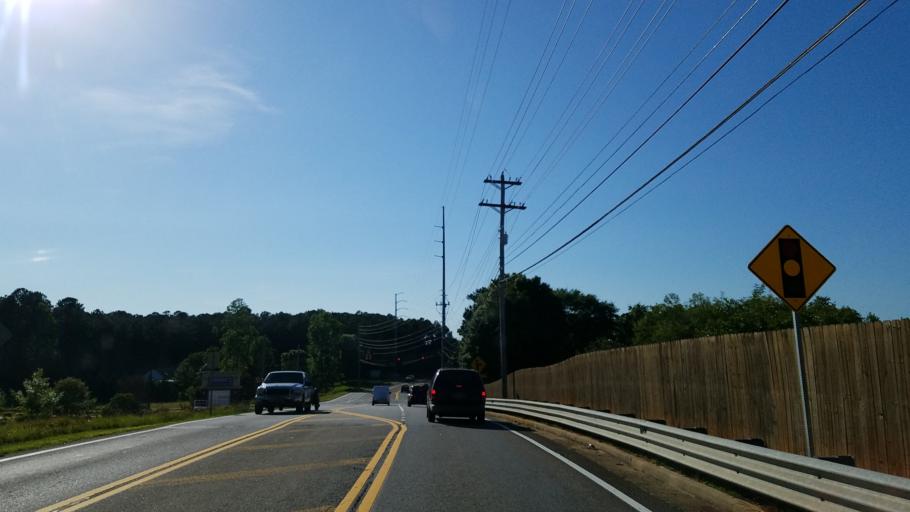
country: US
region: Georgia
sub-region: Cherokee County
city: Woodstock
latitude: 34.1406
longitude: -84.5861
